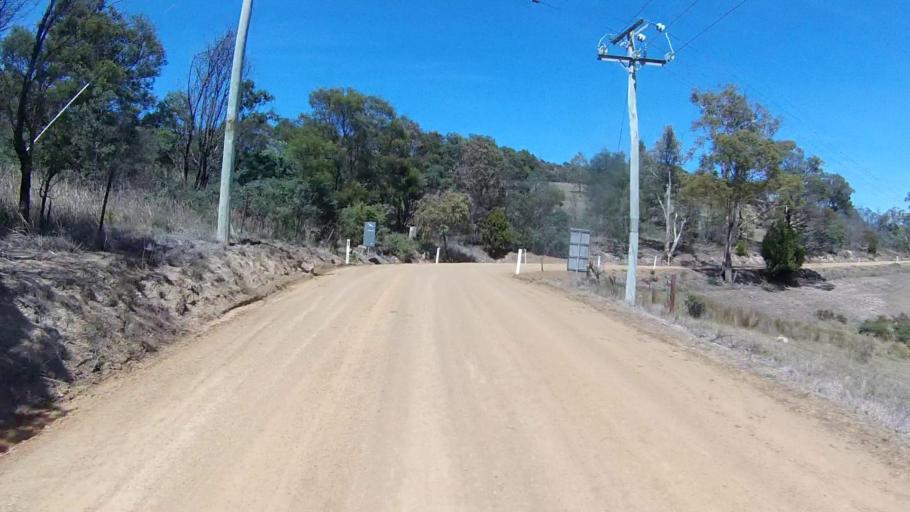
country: AU
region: Tasmania
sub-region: Sorell
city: Sorell
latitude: -42.7806
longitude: 147.6480
